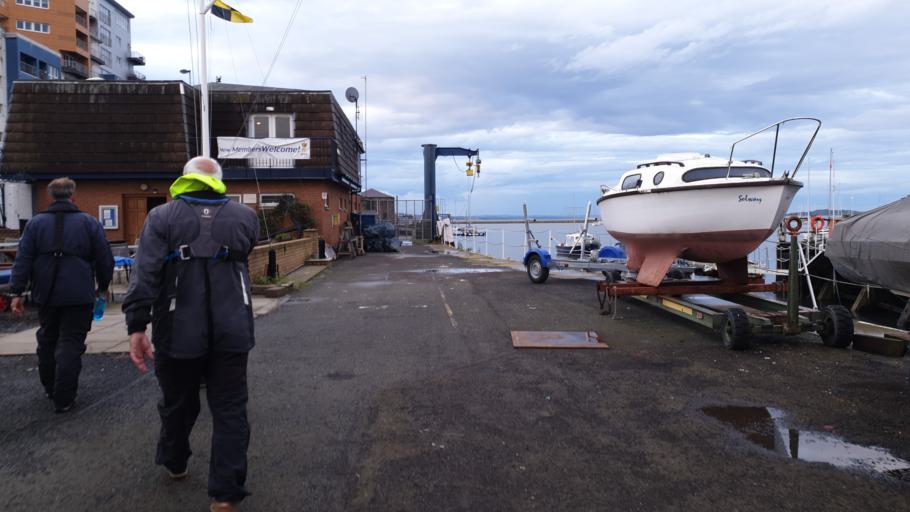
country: GB
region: Scotland
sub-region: Edinburgh
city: Edinburgh
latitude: 55.9827
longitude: -3.2231
